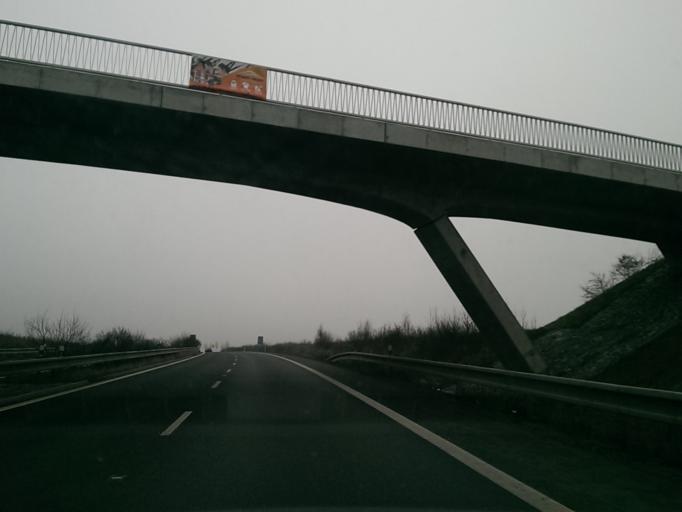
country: CZ
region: Olomoucky
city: Horka nad Moravou
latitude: 49.6028
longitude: 17.2051
